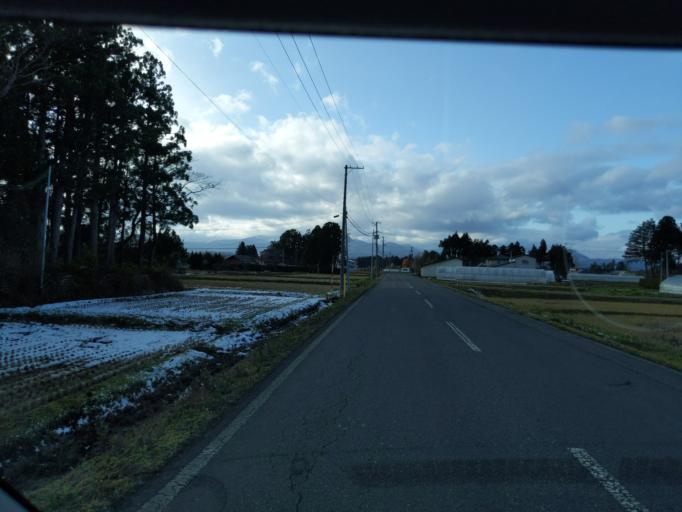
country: JP
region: Iwate
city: Mizusawa
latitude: 39.1875
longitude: 141.0988
